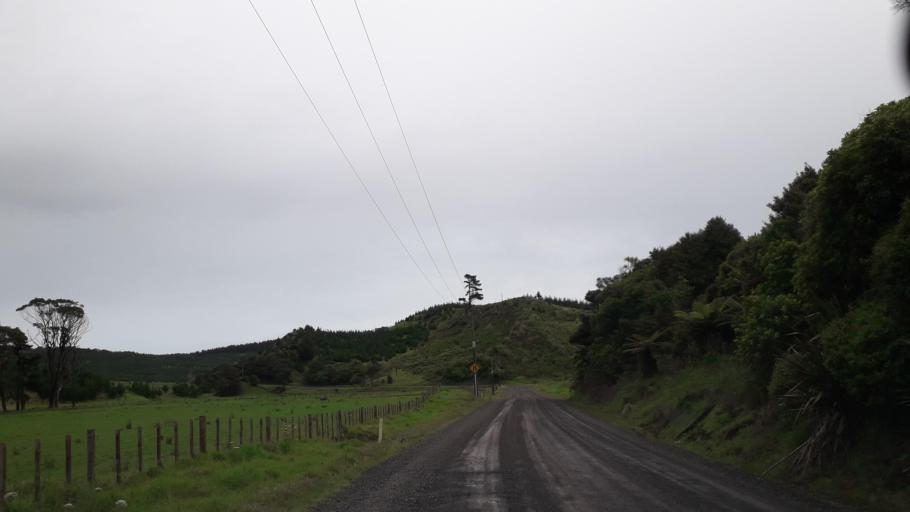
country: NZ
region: Northland
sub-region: Far North District
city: Ahipara
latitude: -35.4304
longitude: 173.3507
